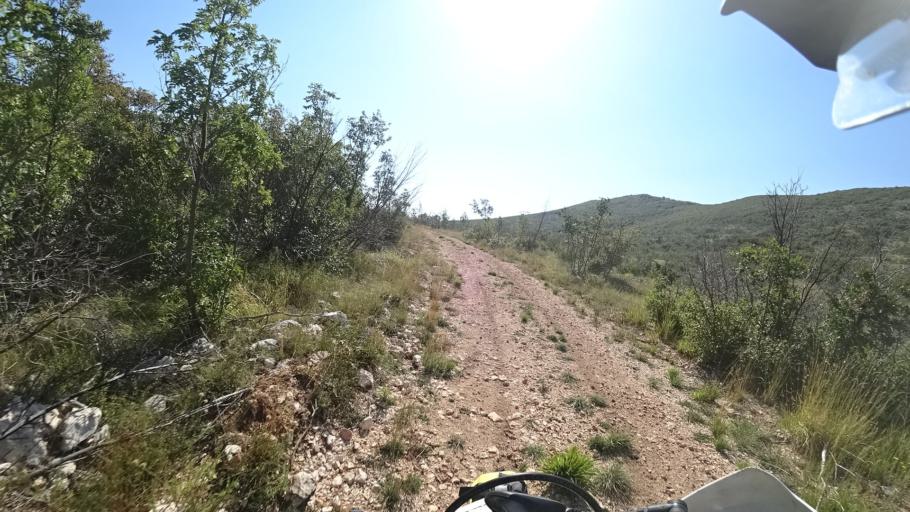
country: HR
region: Sibensko-Kniniska
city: Drnis
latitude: 43.9391
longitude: 16.1593
